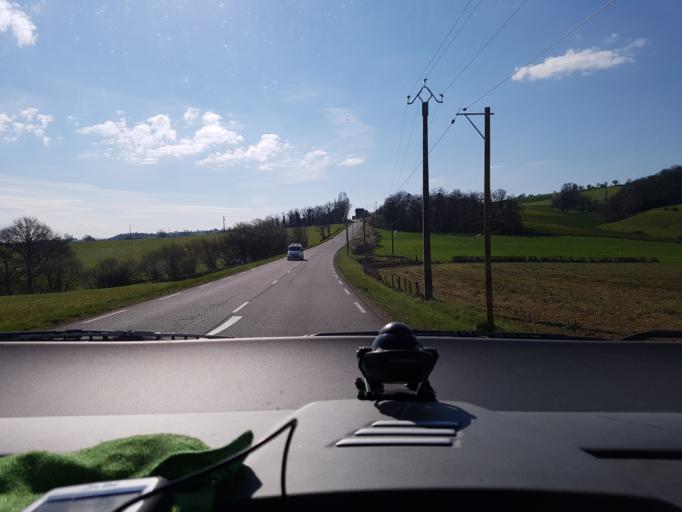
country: FR
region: Midi-Pyrenees
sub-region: Departement de l'Aveyron
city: Moyrazes
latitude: 44.3886
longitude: 2.3986
